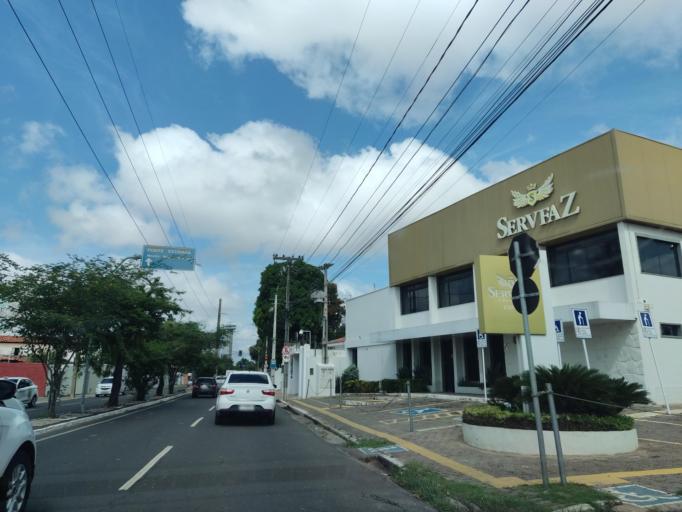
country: BR
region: Piaui
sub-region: Teresina
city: Teresina
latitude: -5.0698
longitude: -42.7952
